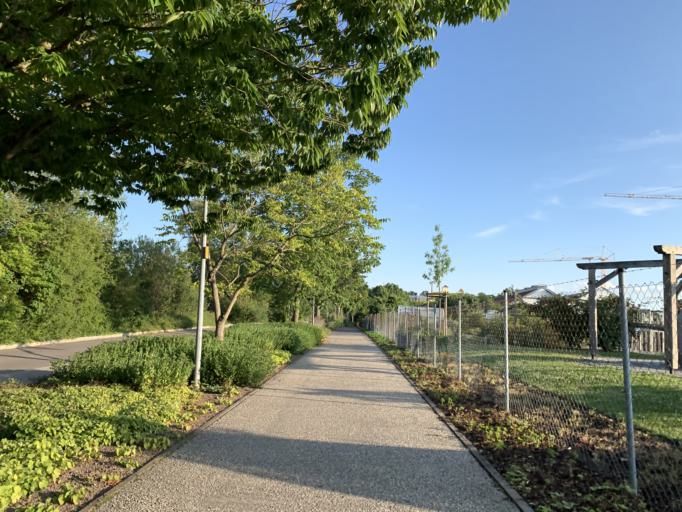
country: DE
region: Bavaria
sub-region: Upper Bavaria
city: Freising
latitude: 48.4037
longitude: 11.7296
